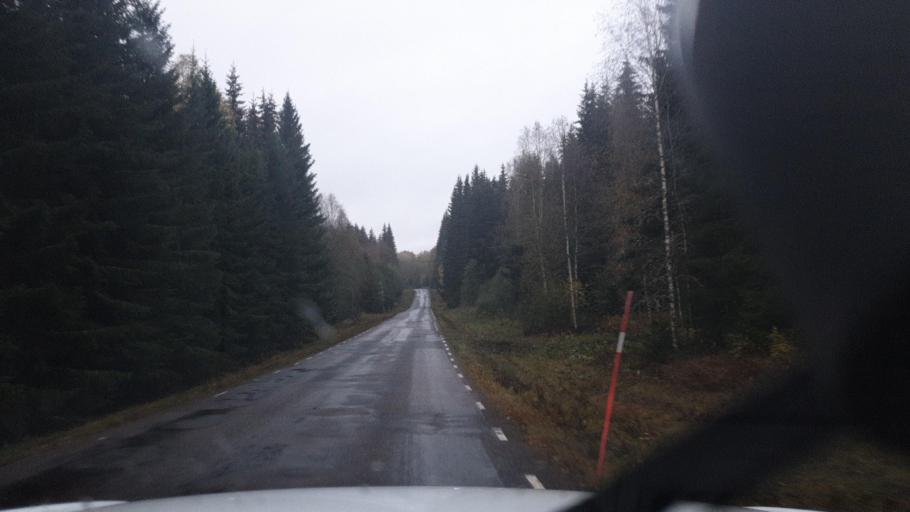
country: SE
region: Vaermland
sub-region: Eda Kommun
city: Amotfors
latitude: 59.8474
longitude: 12.4259
